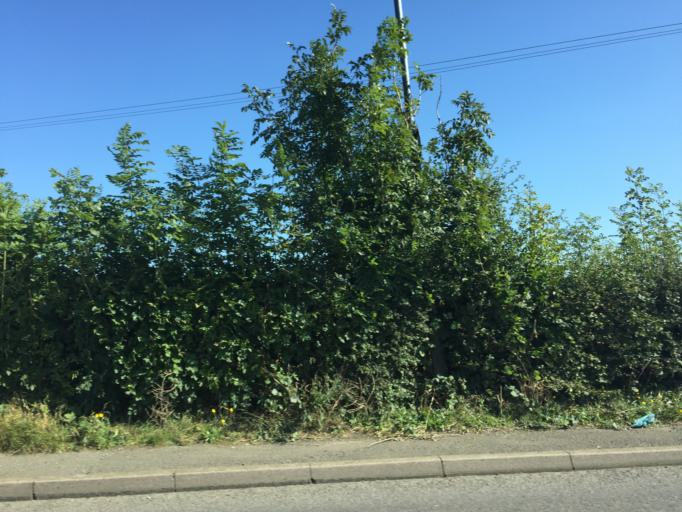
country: GB
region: England
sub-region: South Gloucestershire
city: Tytherington
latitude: 51.5898
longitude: -2.4489
